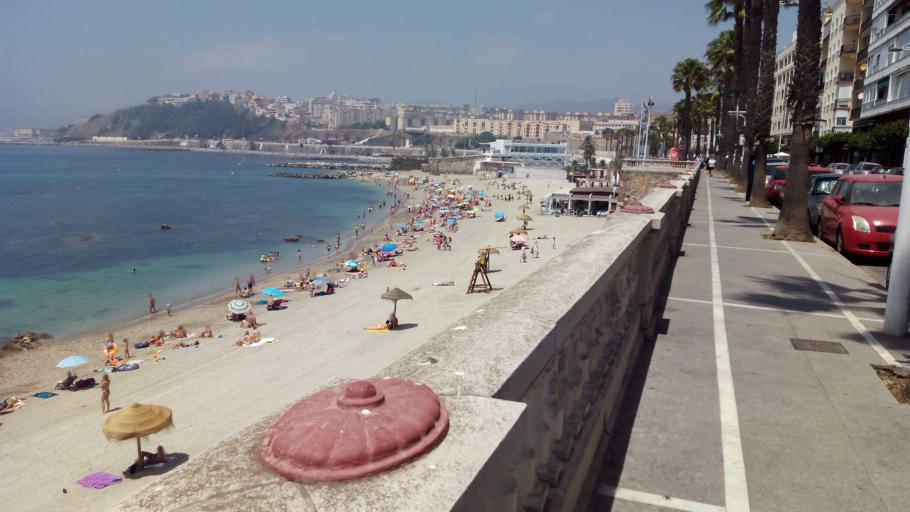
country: ES
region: Ceuta
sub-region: Ceuta
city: Ceuta
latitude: 35.8871
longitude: -5.3138
